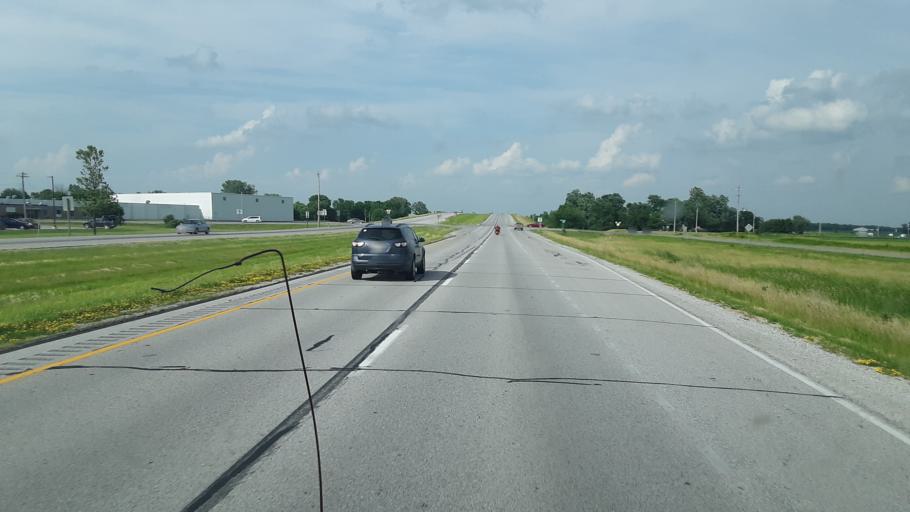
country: US
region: Iowa
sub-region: Polk County
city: Bondurant
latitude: 41.7011
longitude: -93.4448
